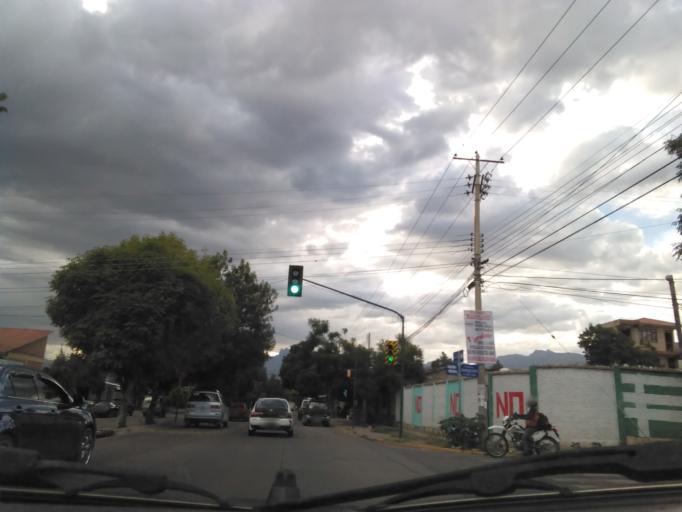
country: BO
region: Cochabamba
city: Cochabamba
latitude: -17.3641
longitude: -66.1647
